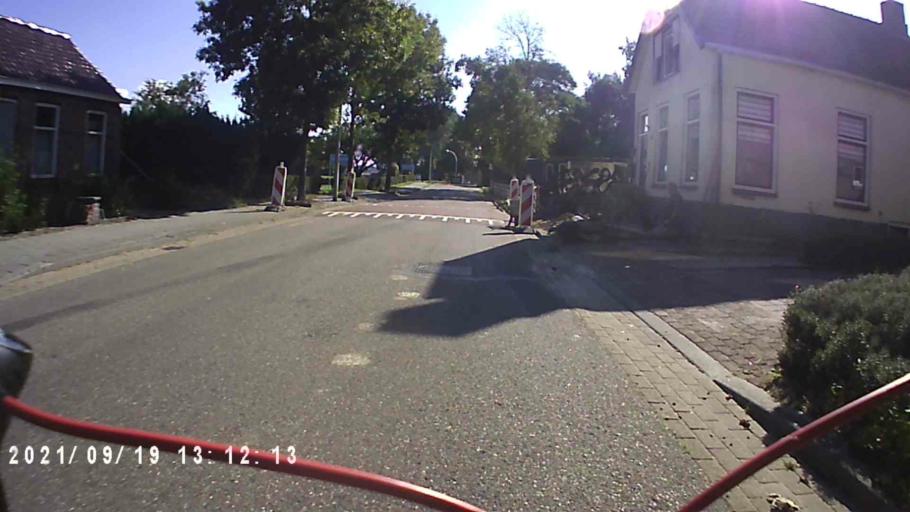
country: NL
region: Groningen
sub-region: Gemeente  Oldambt
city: Winschoten
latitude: 53.1650
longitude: 6.9809
